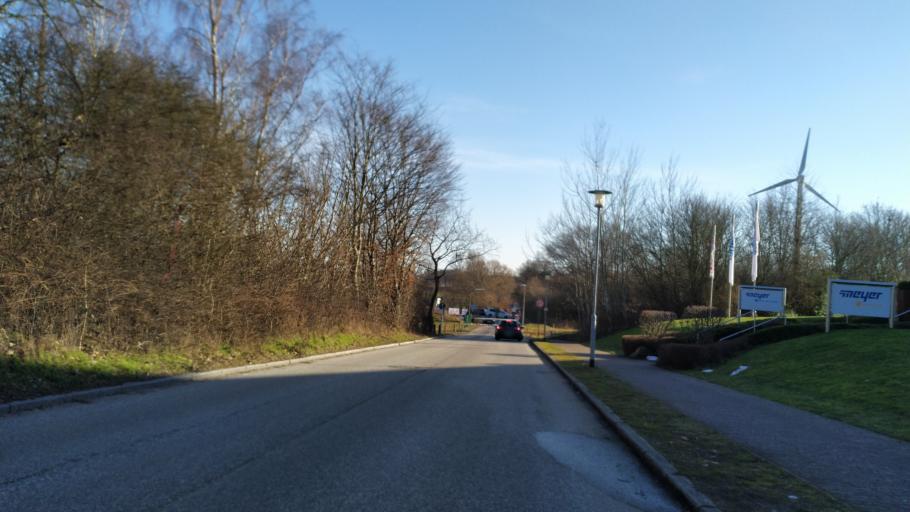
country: DE
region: Schleswig-Holstein
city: Neustadt in Holstein
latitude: 54.0927
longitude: 10.7908
